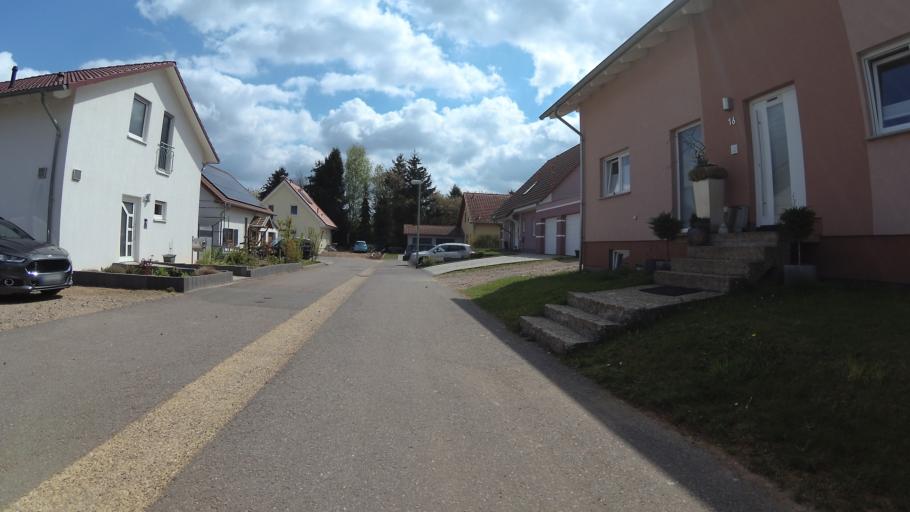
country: DE
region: Saarland
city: Losheim
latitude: 49.5030
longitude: 6.7740
